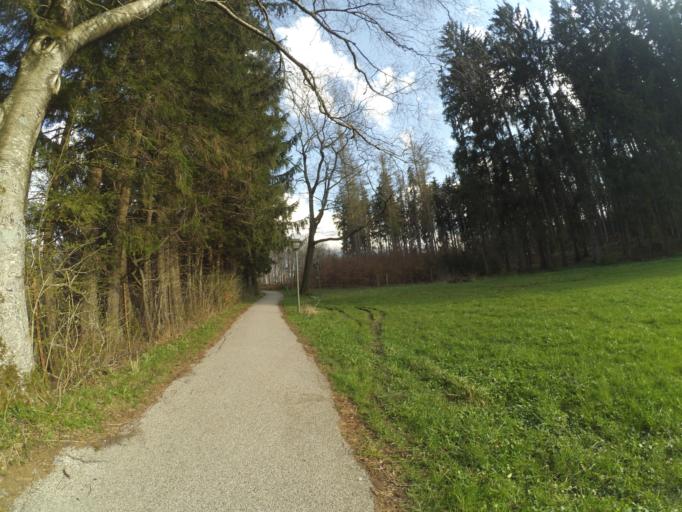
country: DE
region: Bavaria
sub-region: Swabia
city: Bad Worishofen
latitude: 48.0059
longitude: 10.5759
